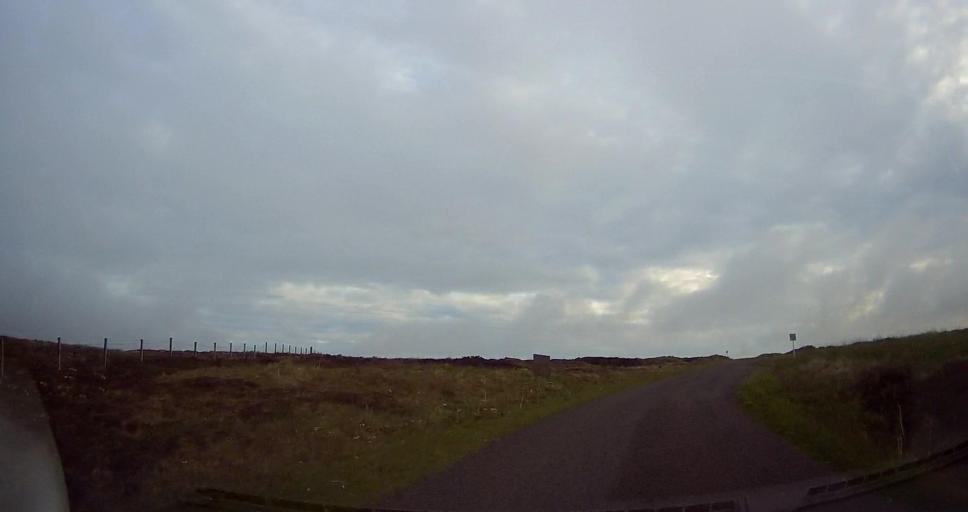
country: GB
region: Scotland
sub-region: Orkney Islands
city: Stromness
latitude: 59.1025
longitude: -3.1362
